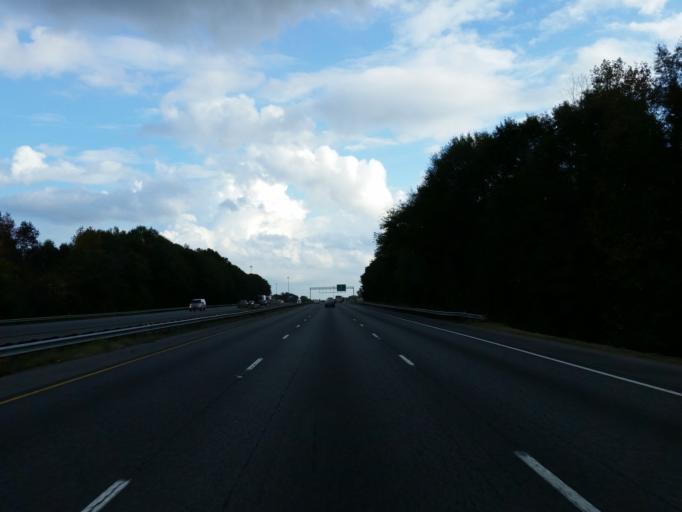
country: US
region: Georgia
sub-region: Butts County
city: Jackson
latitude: 33.2141
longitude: -84.0661
